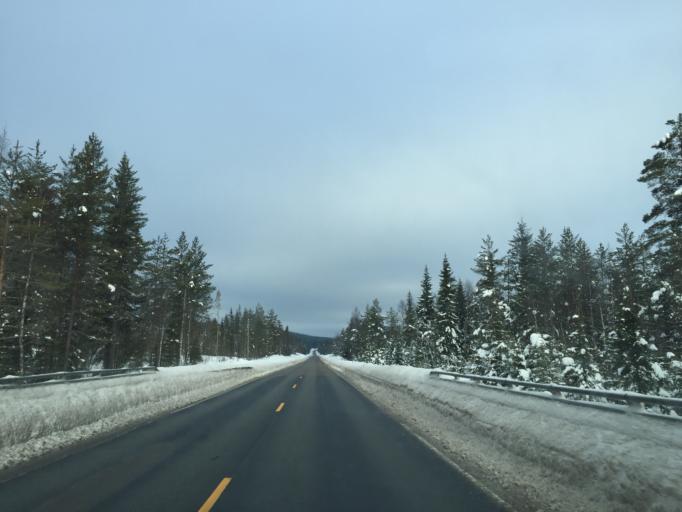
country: NO
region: Hedmark
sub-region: Trysil
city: Innbygda
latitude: 61.1576
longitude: 12.1392
